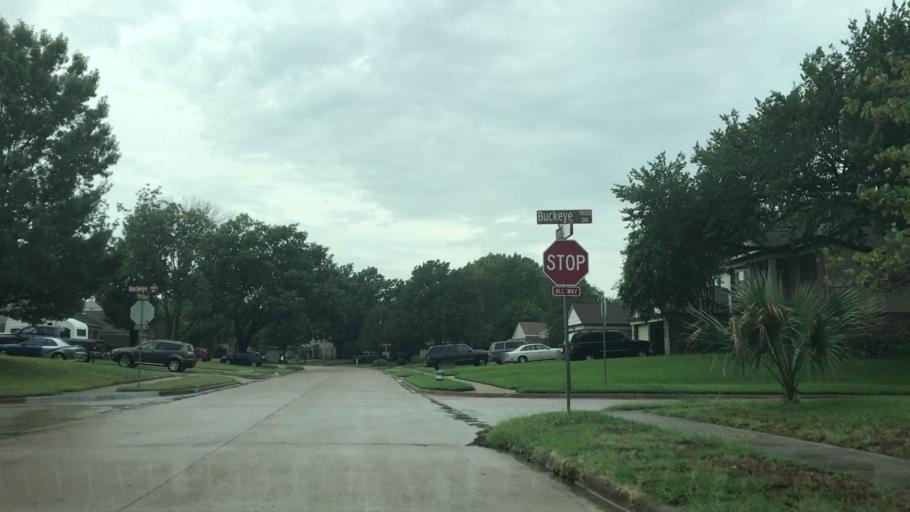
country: US
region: Texas
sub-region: Denton County
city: Flower Mound
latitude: 33.0397
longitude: -97.0578
